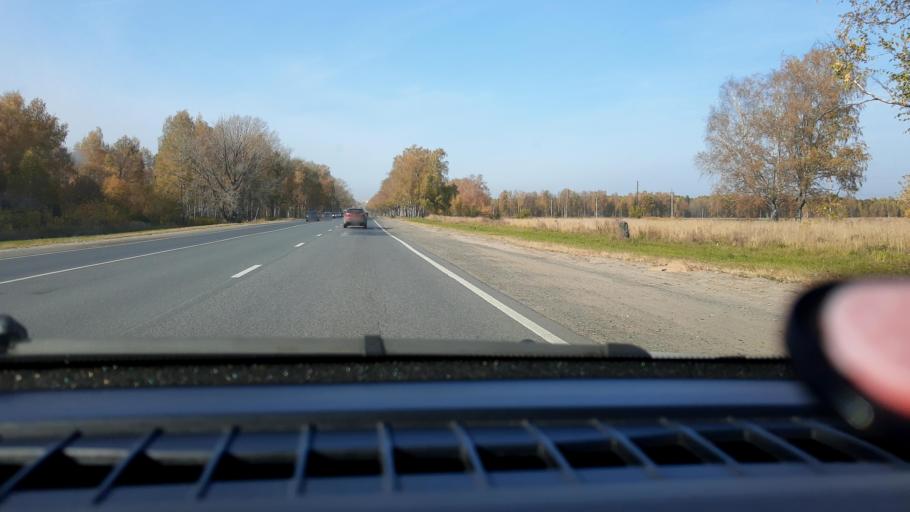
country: RU
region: Nizjnij Novgorod
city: Kstovo
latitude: 56.1339
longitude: 44.2452
